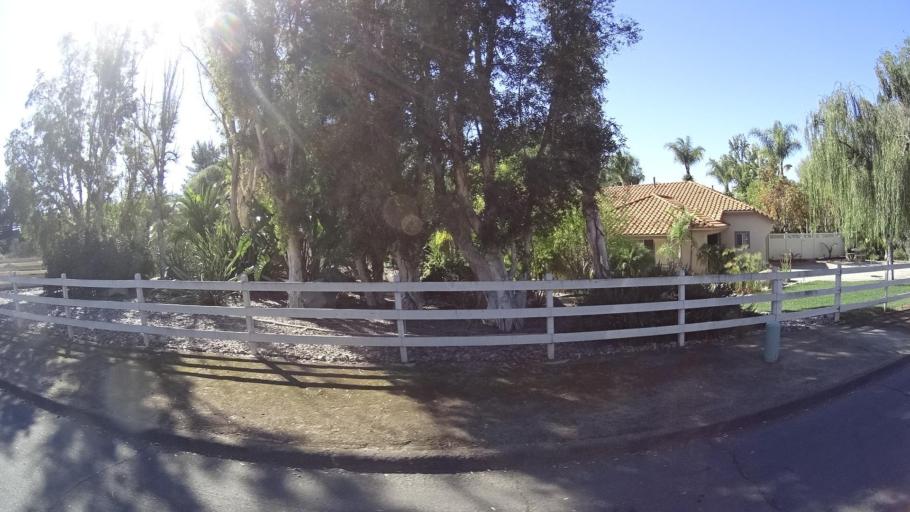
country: US
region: California
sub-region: San Diego County
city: Jamul
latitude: 32.7401
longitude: -116.8601
